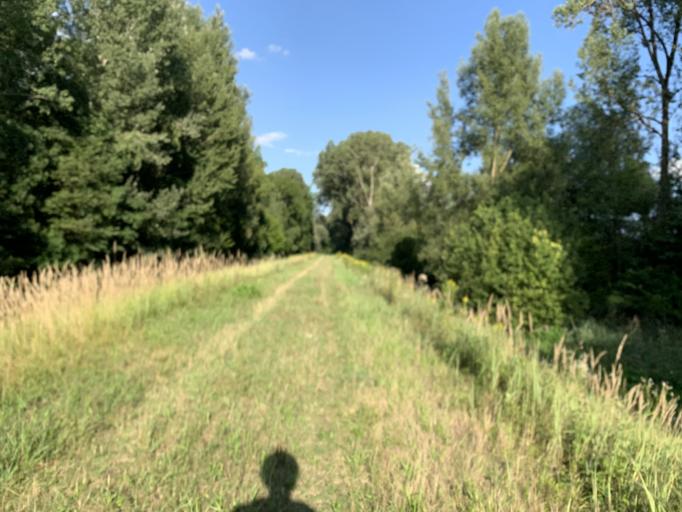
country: DE
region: Bavaria
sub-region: Upper Bavaria
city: Marzling
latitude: 48.4006
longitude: 11.7859
